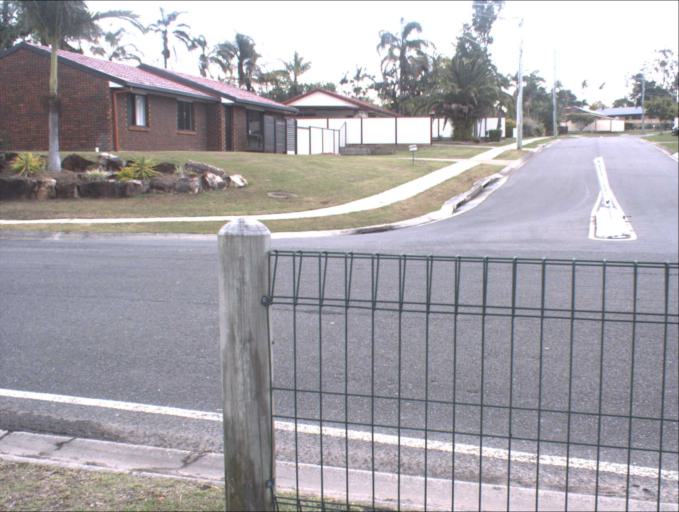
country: AU
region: Queensland
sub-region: Brisbane
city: Sunnybank Hills
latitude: -27.6685
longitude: 153.0474
